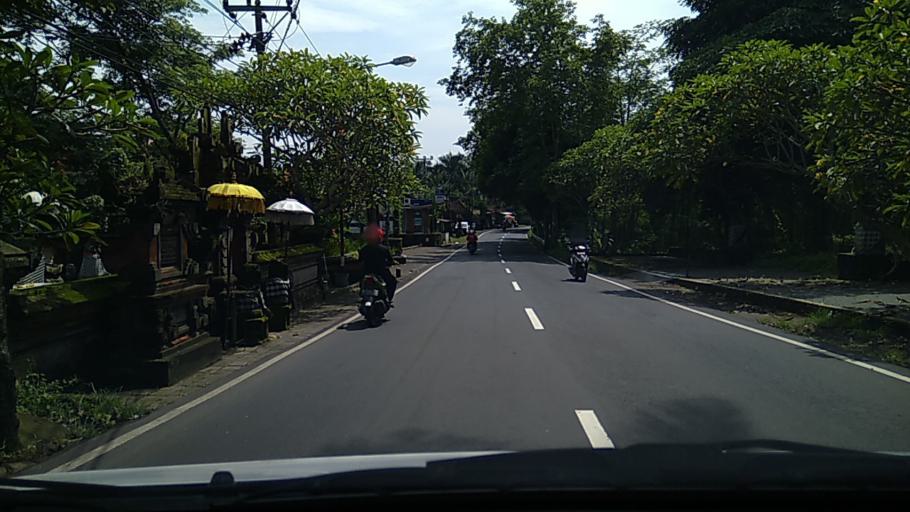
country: ID
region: Bali
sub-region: Kabupaten Gianyar
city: Ubud
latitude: -8.5228
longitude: 115.2792
